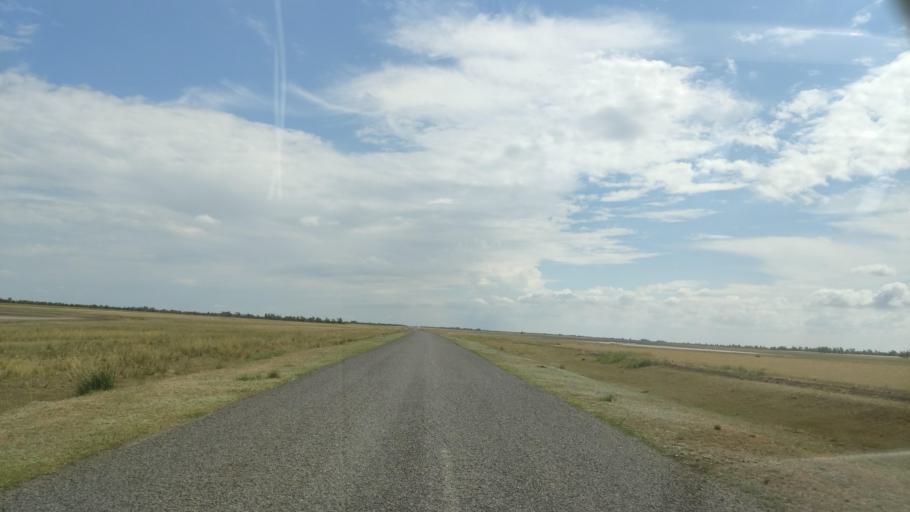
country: KZ
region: Pavlodar
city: Pavlodar
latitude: 52.6354
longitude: 76.9170
